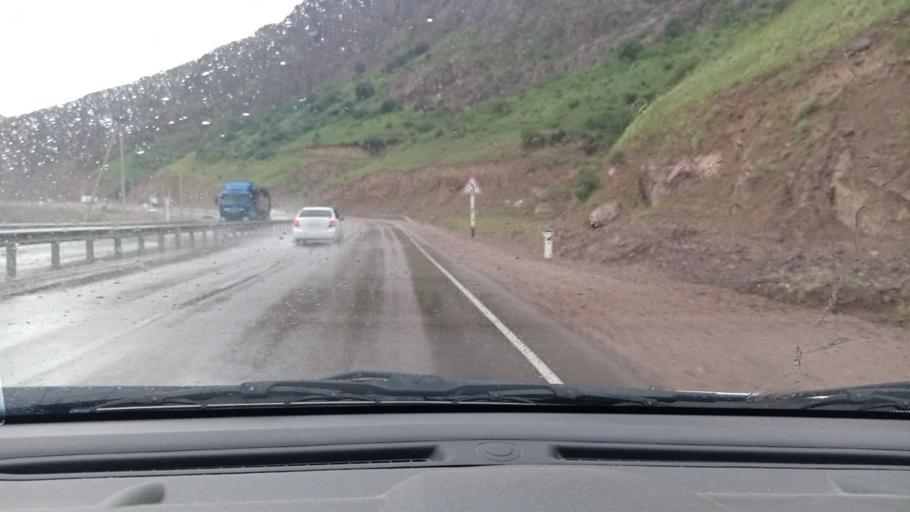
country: UZ
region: Toshkent
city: Angren
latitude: 41.0775
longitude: 70.3187
